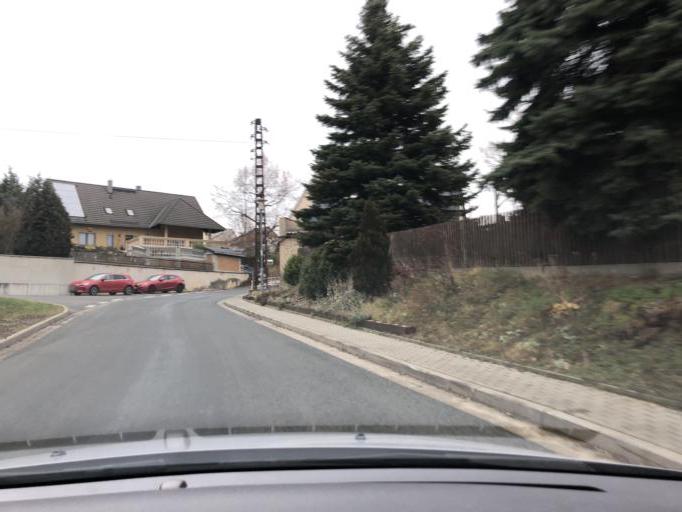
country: DE
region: Saxony
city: Rosswein
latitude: 51.0761
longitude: 13.2387
